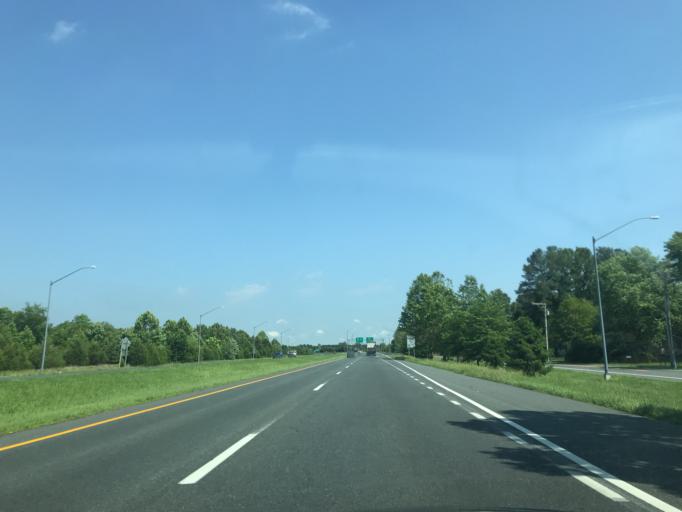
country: US
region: Maryland
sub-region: Wicomico County
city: Hebron
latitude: 38.4052
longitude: -75.6369
